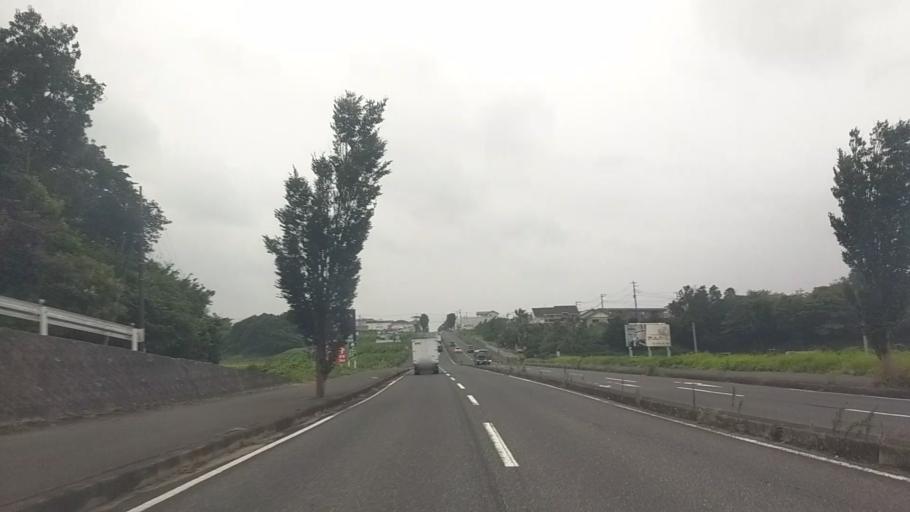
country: JP
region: Chiba
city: Kisarazu
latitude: 35.3849
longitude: 139.9692
